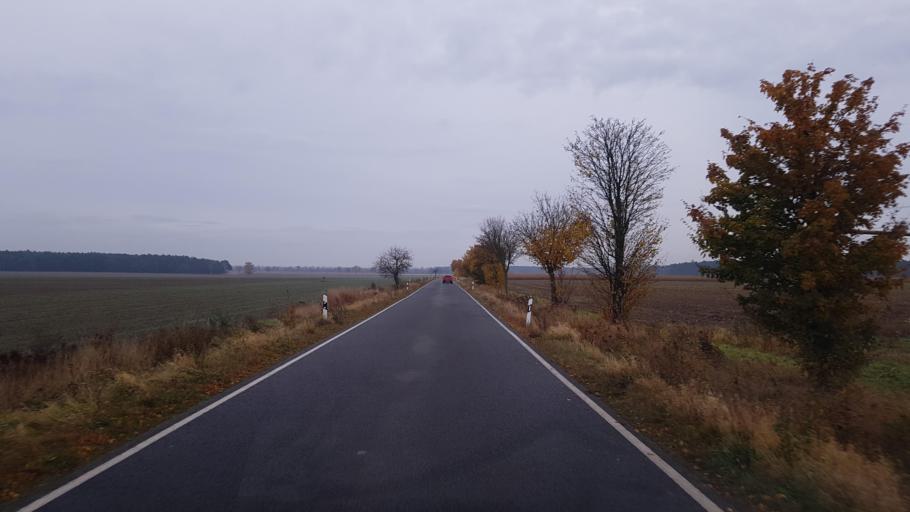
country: DE
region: Saxony-Anhalt
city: Seyda
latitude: 51.9223
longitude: 12.8940
